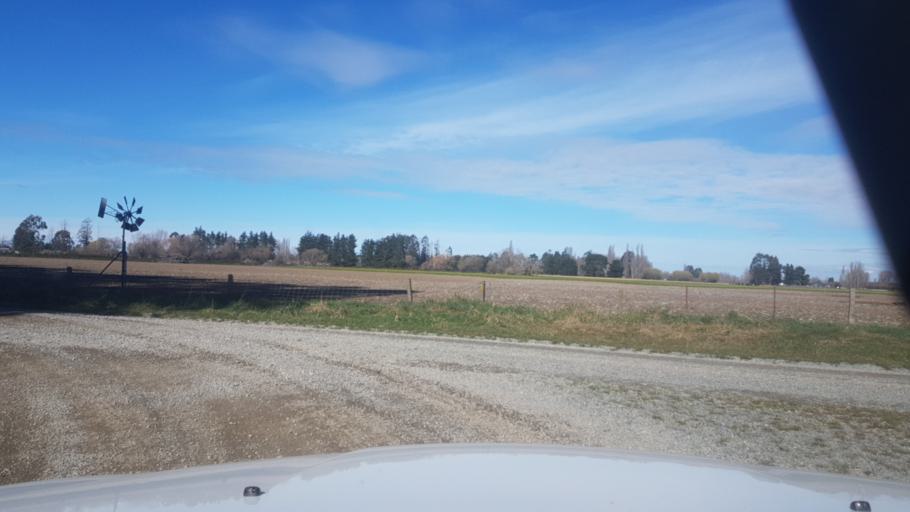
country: NZ
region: Canterbury
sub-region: Timaru District
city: Pleasant Point
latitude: -44.1442
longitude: 171.2739
